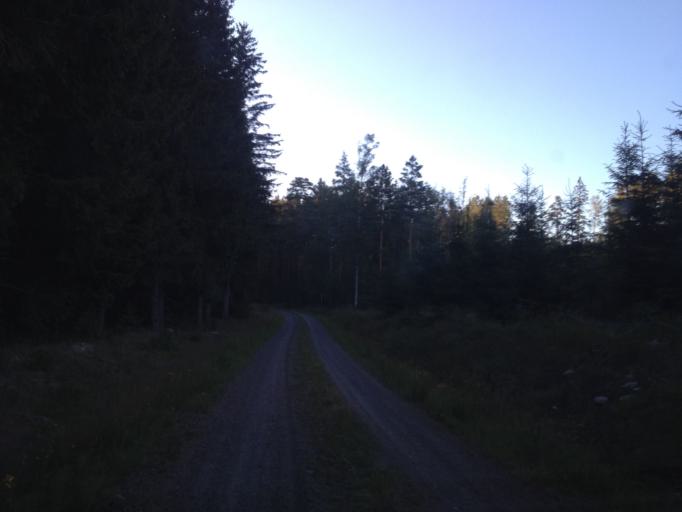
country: SE
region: Kalmar
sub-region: Vasterviks Kommun
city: Overum
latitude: 58.0042
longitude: 16.1220
